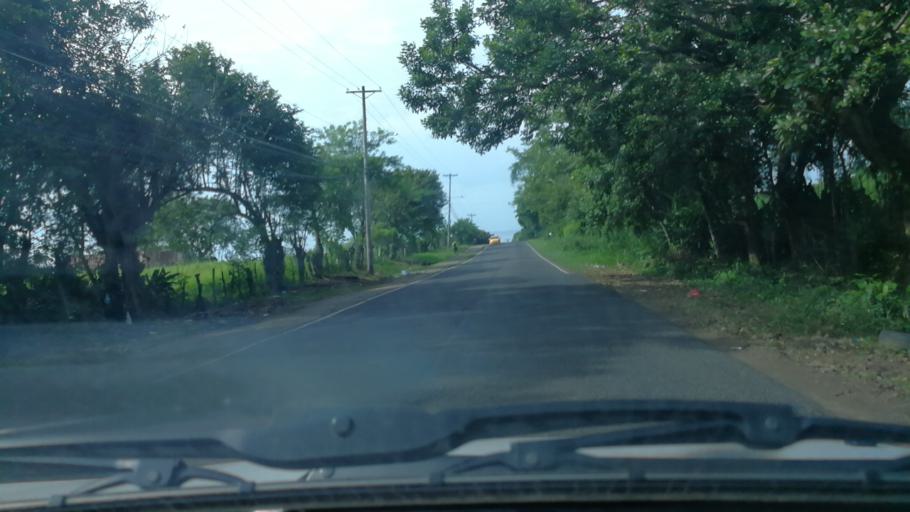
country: PA
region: Panama
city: Pacora
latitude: 9.0931
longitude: -79.2884
